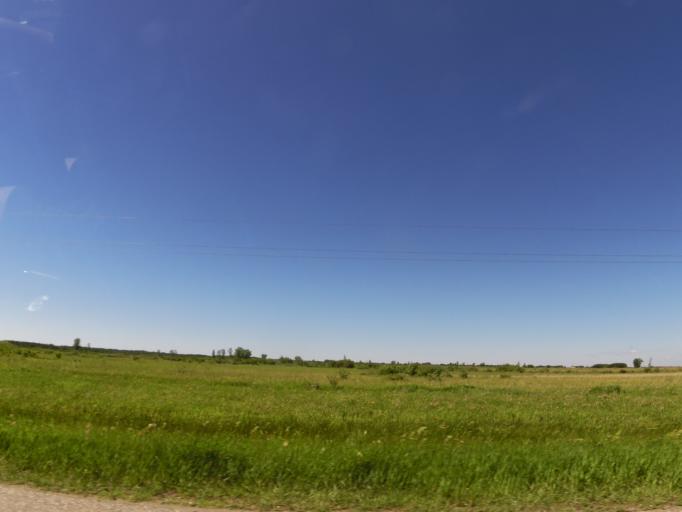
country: US
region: Minnesota
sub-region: Red Lake County
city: Red Lake Falls
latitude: 47.7247
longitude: -96.1920
